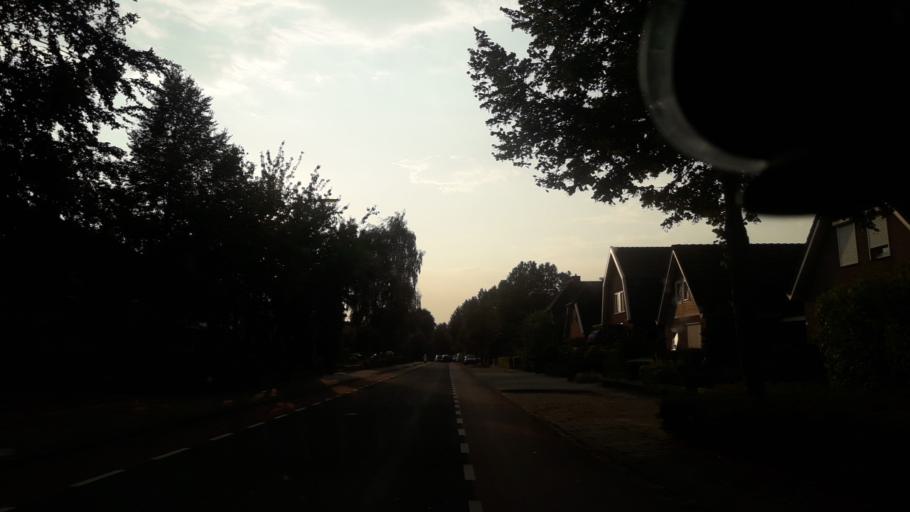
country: NL
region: Gelderland
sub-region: Oude IJsselstreek
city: Varsseveld
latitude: 51.9456
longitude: 6.4539
